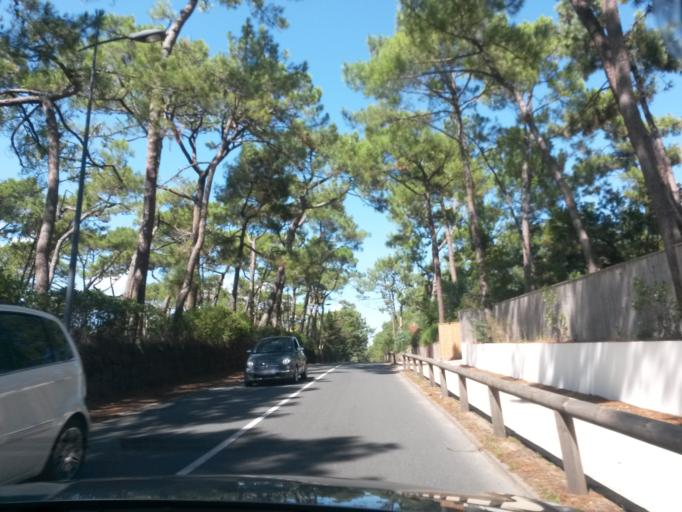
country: FR
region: Aquitaine
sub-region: Departement de la Gironde
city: Arcachon
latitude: 44.6594
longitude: -1.2440
